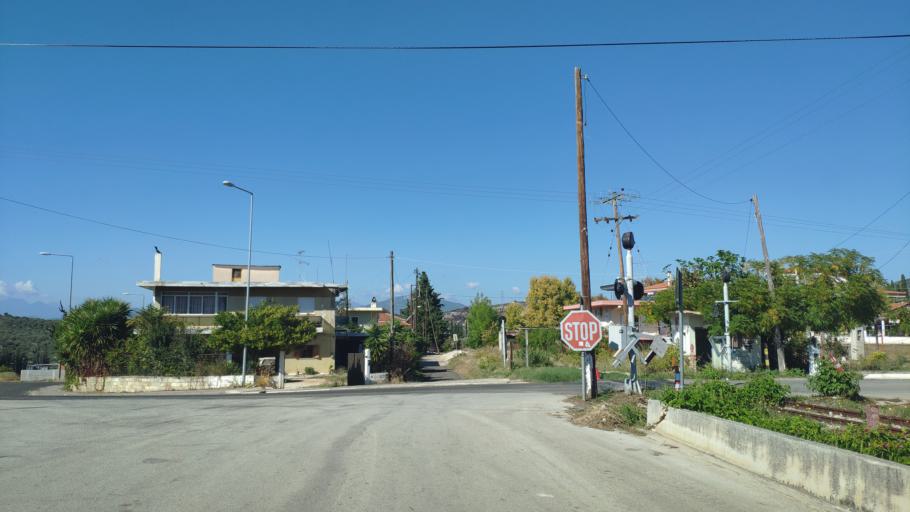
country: GR
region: Peloponnese
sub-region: Nomos Korinthias
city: Khiliomodhi
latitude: 37.8080
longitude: 22.8660
